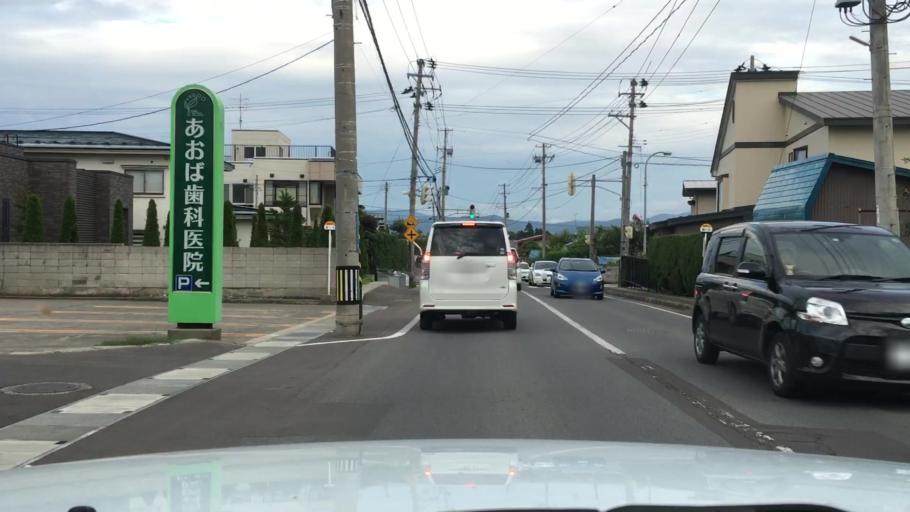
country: JP
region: Aomori
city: Hirosaki
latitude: 40.5868
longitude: 140.4616
